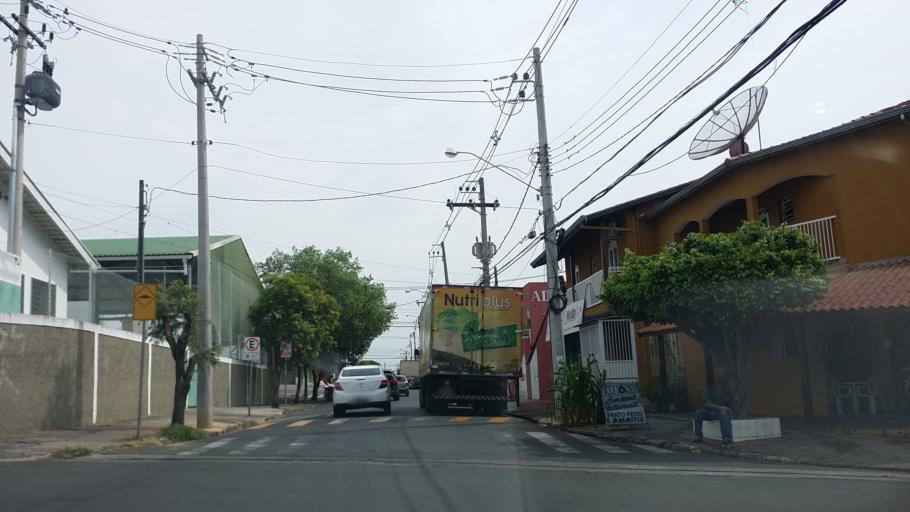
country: BR
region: Sao Paulo
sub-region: Indaiatuba
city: Indaiatuba
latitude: -23.1190
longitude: -47.2381
